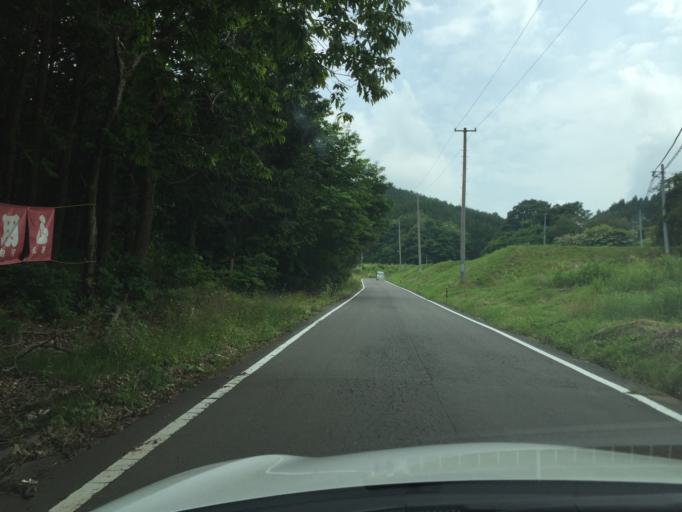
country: JP
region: Fukushima
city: Sukagawa
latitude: 37.2625
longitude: 140.5000
